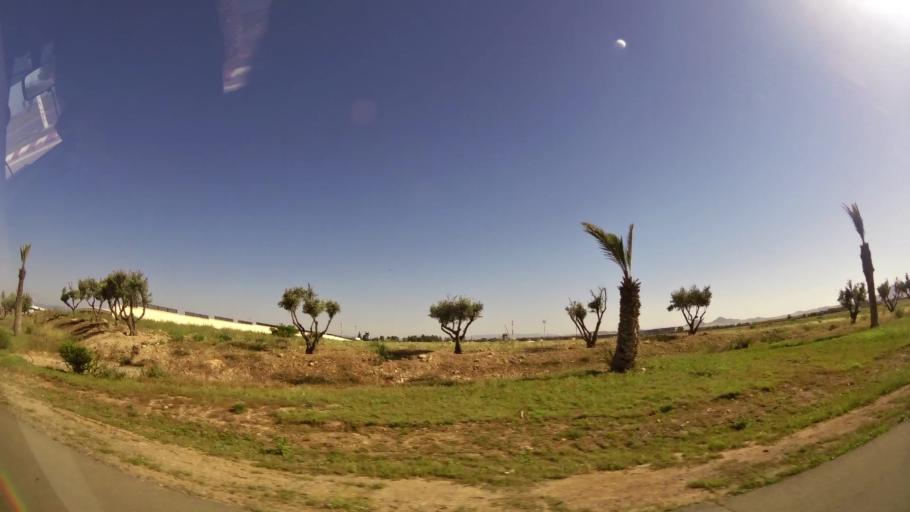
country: MA
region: Oriental
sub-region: Oujda-Angad
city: Oujda
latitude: 34.7911
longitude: -1.9453
